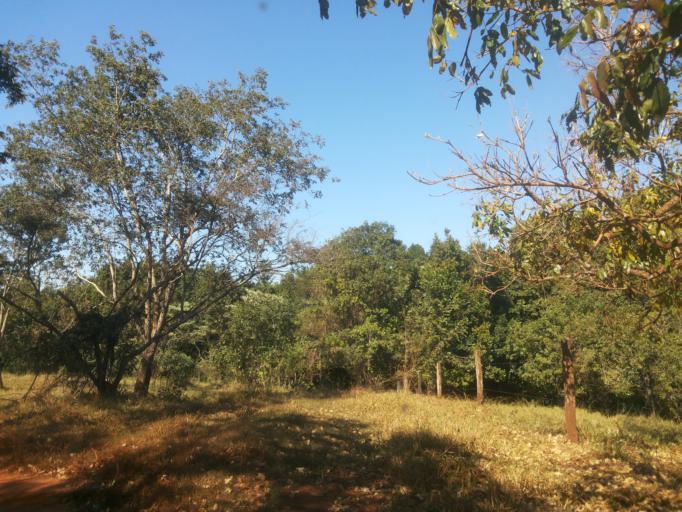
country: BR
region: Minas Gerais
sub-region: Centralina
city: Centralina
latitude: -18.7326
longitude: -49.1779
